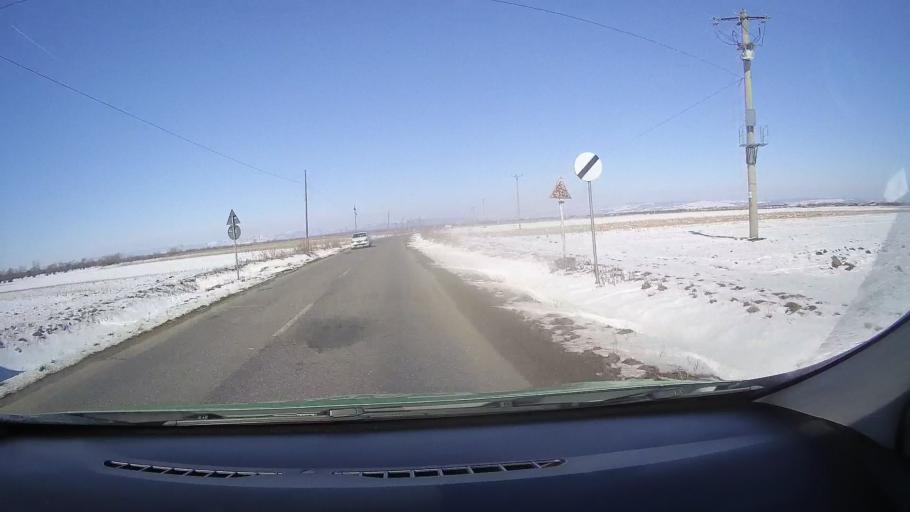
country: RO
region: Brasov
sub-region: Comuna Harseni
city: Harseni
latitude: 45.7597
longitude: 25.0088
